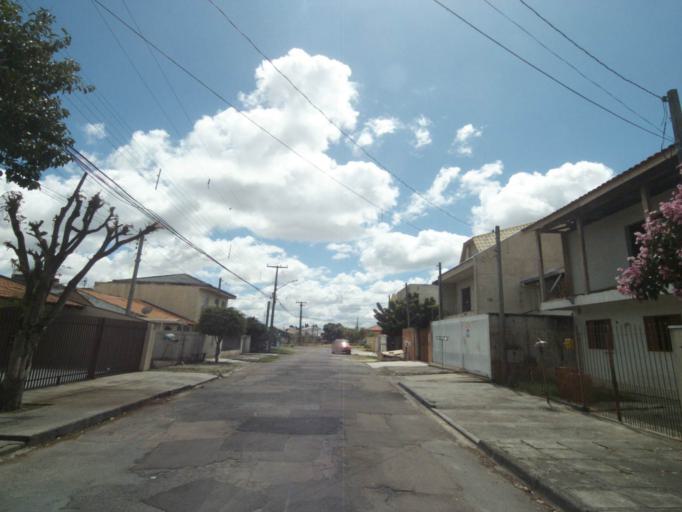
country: BR
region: Parana
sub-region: Pinhais
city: Pinhais
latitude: -25.4416
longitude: -49.2031
